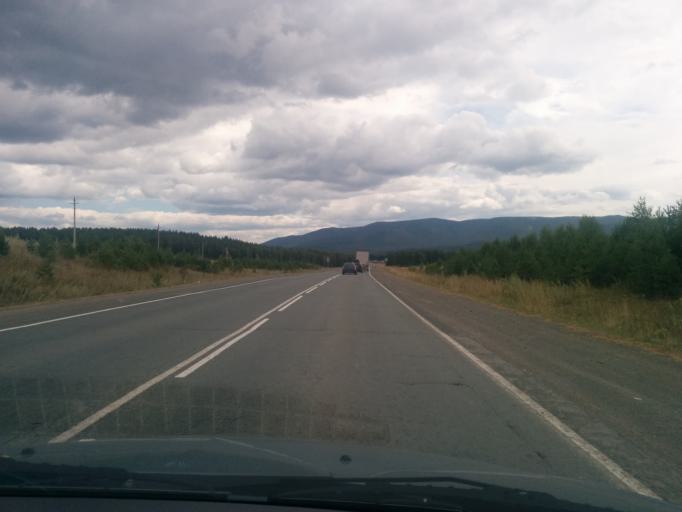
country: RU
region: Bashkortostan
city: Lomovka
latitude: 53.8939
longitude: 58.0929
